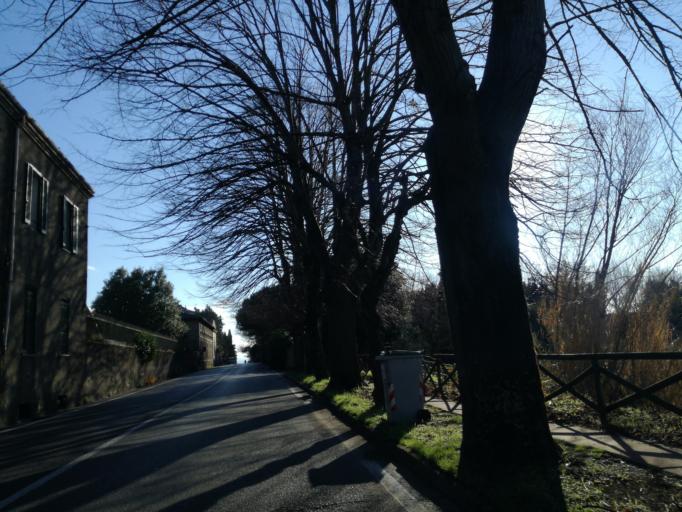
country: IT
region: Umbria
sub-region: Provincia di Perugia
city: Perugia
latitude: 43.0909
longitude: 12.3981
